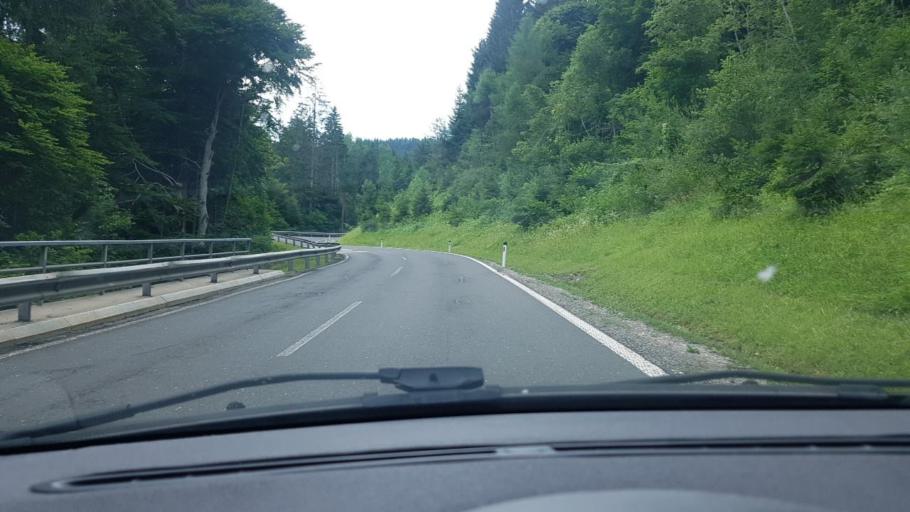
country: AT
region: Carinthia
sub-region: Politischer Bezirk Spittal an der Drau
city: Greifenburg
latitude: 46.7341
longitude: 13.2224
